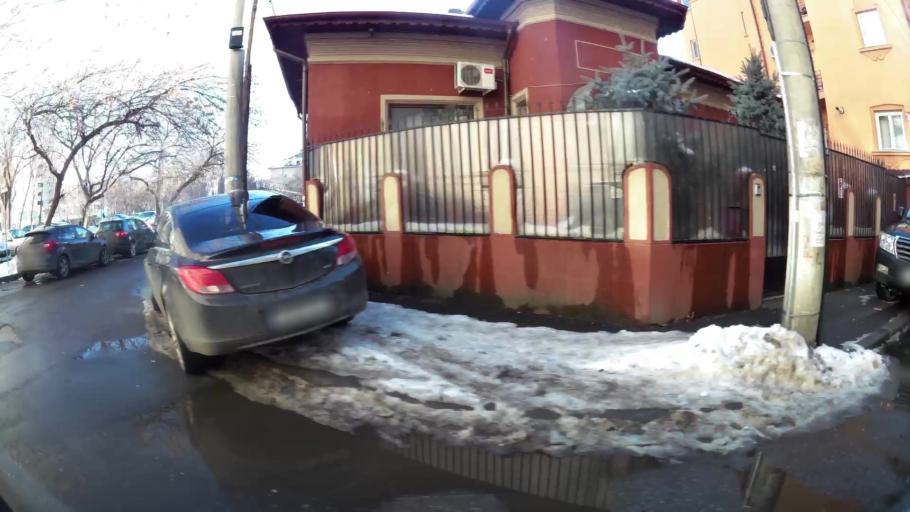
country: RO
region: Bucuresti
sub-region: Municipiul Bucuresti
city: Bucuresti
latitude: 44.4246
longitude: 26.0800
